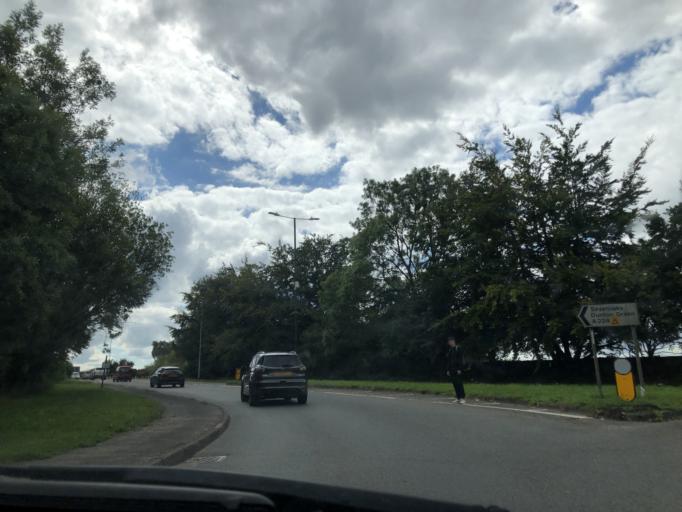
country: GB
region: England
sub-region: Kent
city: Halstead
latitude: 51.3327
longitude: 0.1483
